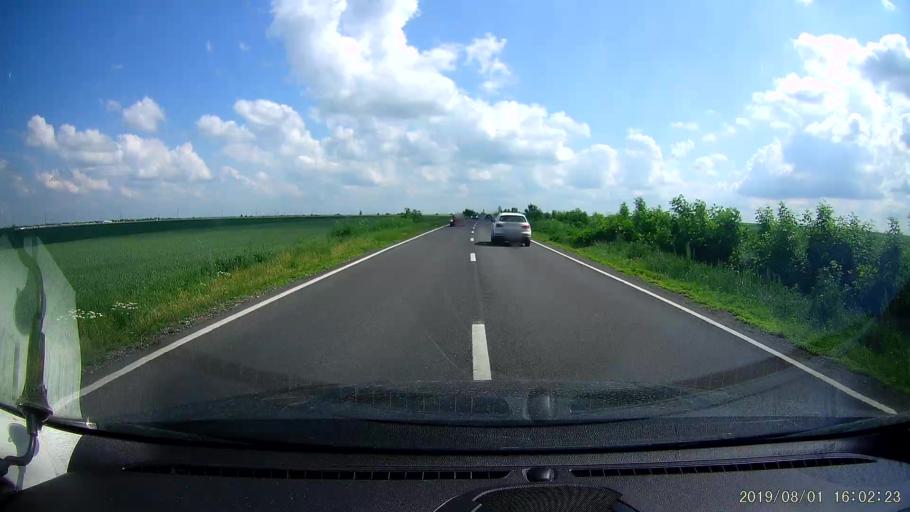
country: RO
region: Ialomita
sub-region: Comuna Ciulnita
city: Ciulnita
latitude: 44.4909
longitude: 27.3875
